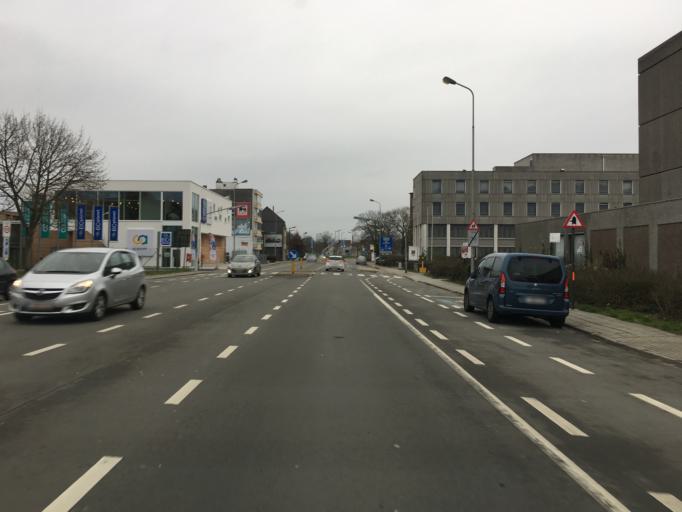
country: BE
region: Flanders
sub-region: Provincie West-Vlaanderen
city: Kortrijk
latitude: 50.8356
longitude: 3.2647
